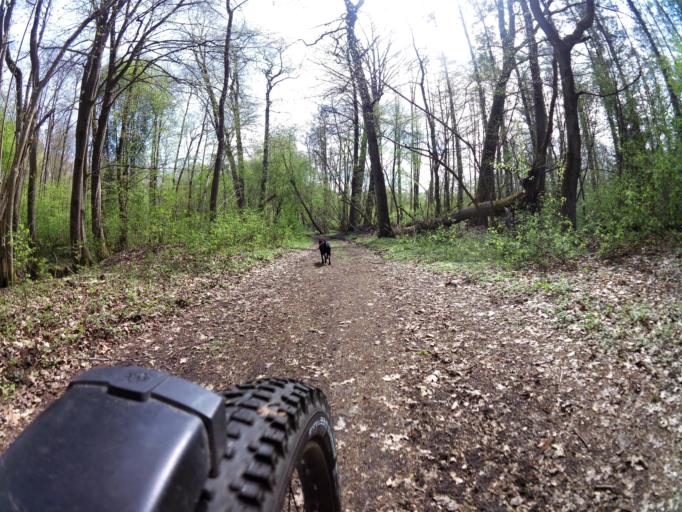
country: PL
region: West Pomeranian Voivodeship
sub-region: Powiat gryficki
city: Ploty
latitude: 53.7504
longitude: 15.3127
